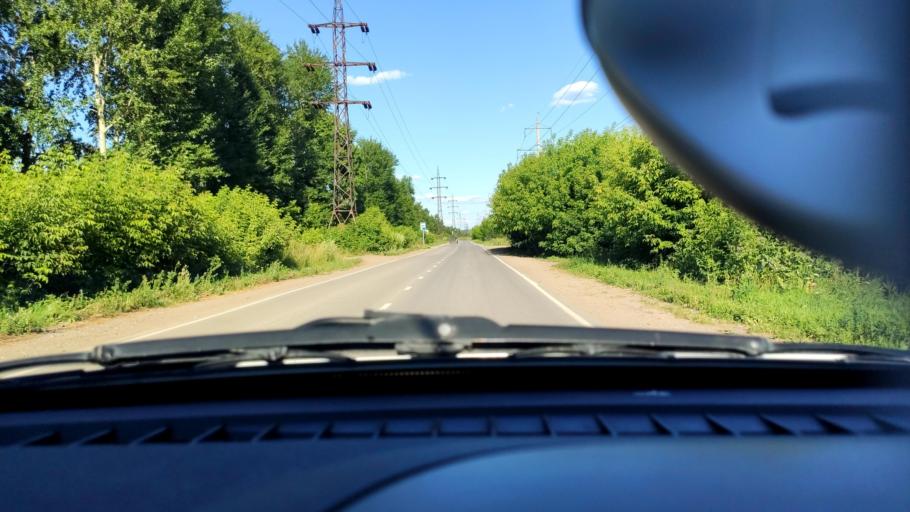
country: RU
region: Perm
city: Krasnokamsk
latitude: 58.0744
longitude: 55.7983
